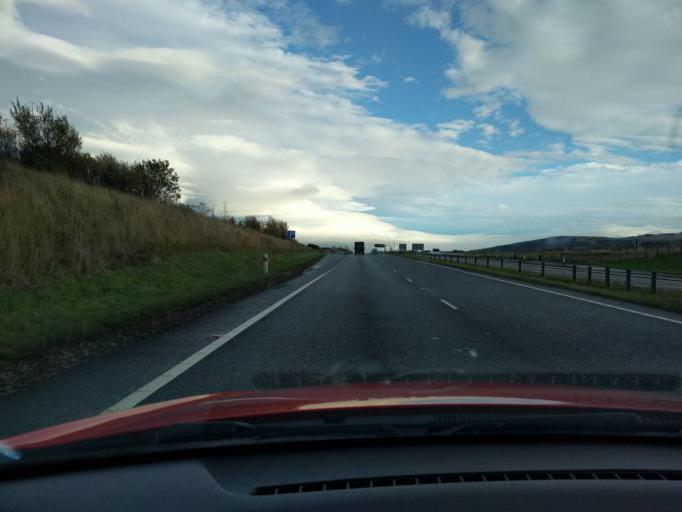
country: GB
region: Scotland
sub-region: East Lothian
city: Dunbar
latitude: 55.9889
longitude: -2.5564
